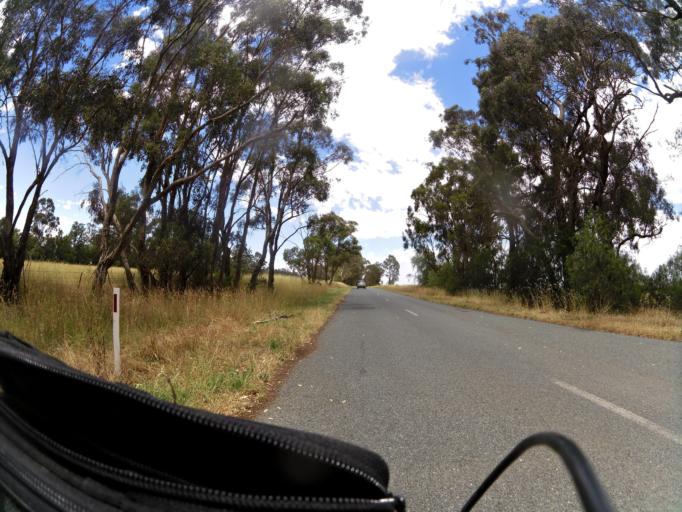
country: AU
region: Victoria
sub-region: Greater Shepparton
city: Shepparton
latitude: -36.6563
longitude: 145.2004
